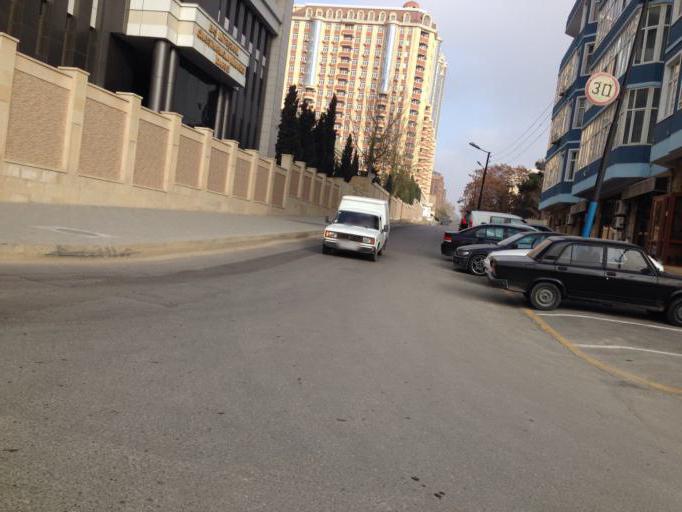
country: AZ
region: Baki
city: Baku
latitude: 40.3951
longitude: 49.8574
